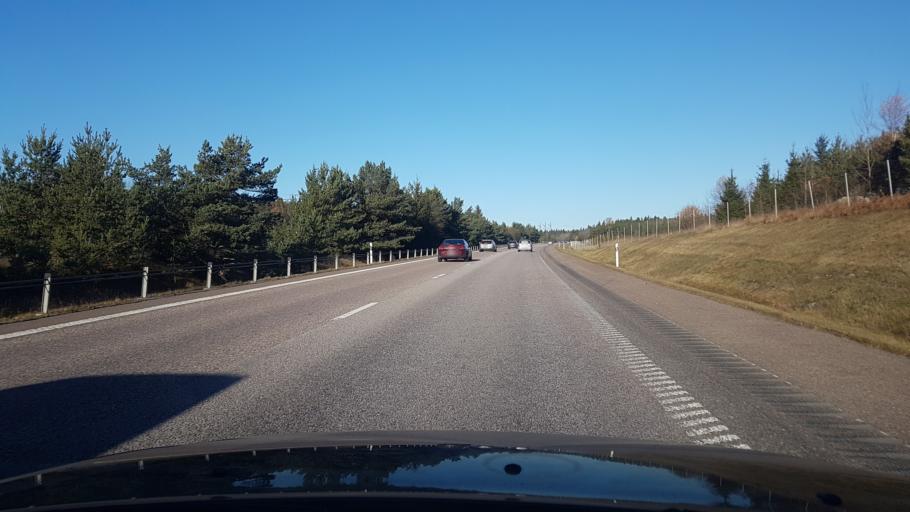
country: SE
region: Stockholm
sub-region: Sigtuna Kommun
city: Marsta
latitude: 59.6805
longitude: 17.8693
